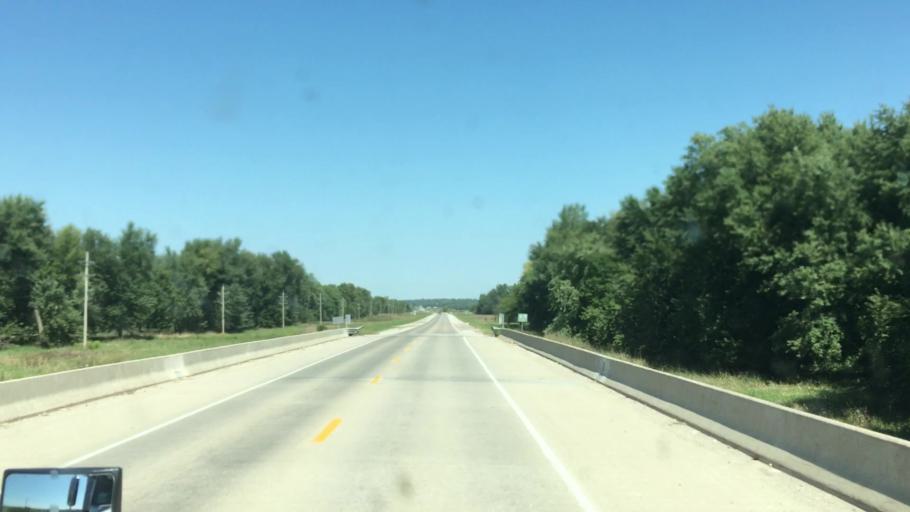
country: US
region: Iowa
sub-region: Benton County
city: Belle Plaine
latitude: 41.8598
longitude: -92.2779
